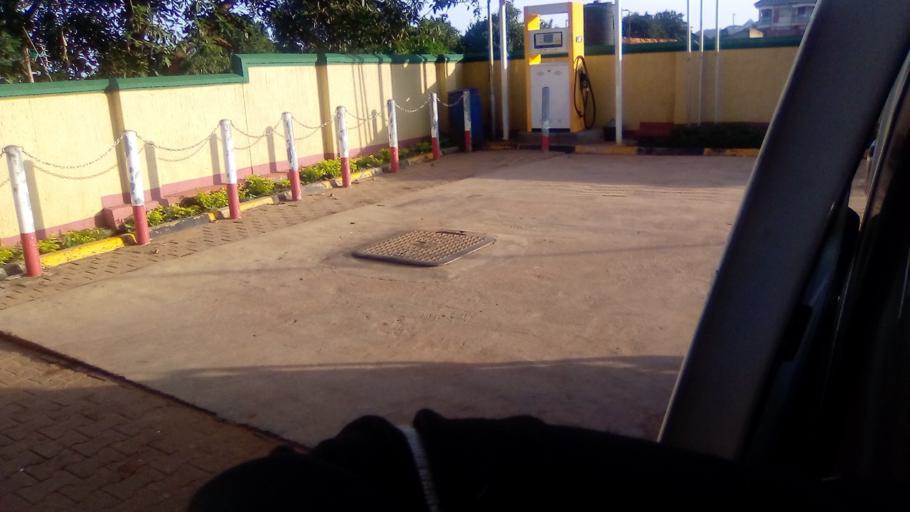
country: UG
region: Central Region
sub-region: Wakiso District
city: Kajansi
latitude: 0.1984
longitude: 32.5400
